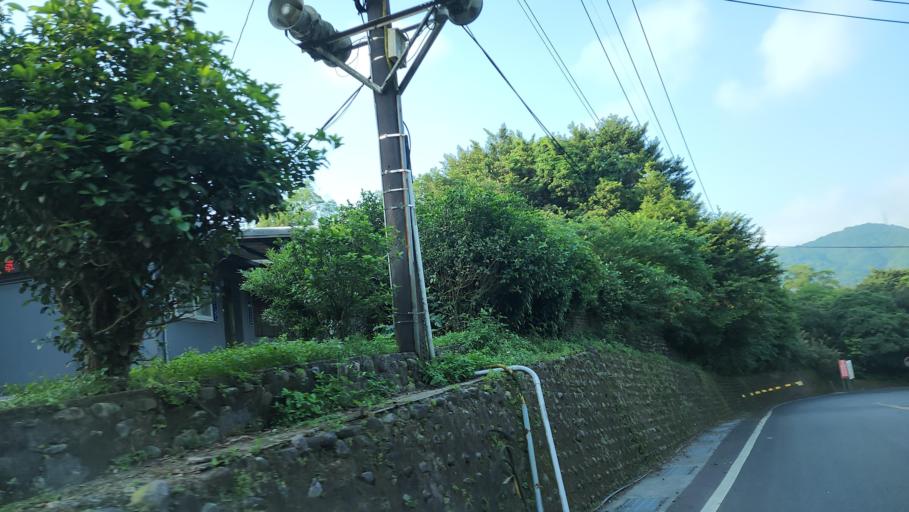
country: TW
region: Taiwan
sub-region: Keelung
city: Keelung
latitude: 25.1768
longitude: 121.6510
